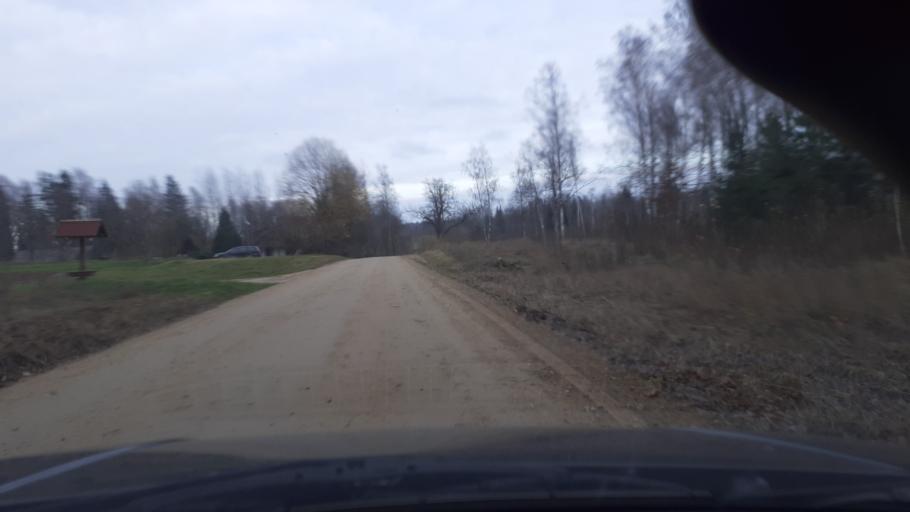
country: LV
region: Alsunga
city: Alsunga
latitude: 56.9492
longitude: 21.6423
